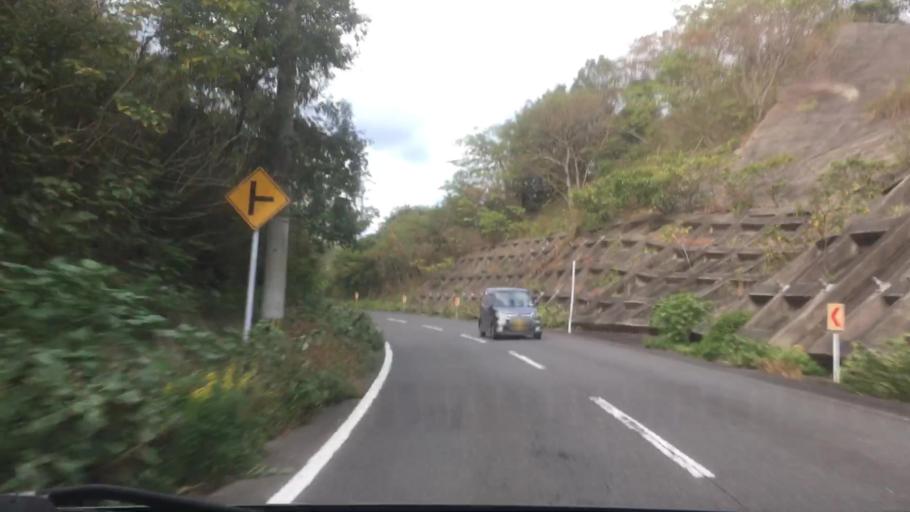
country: JP
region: Nagasaki
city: Sasebo
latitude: 32.9964
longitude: 129.7197
